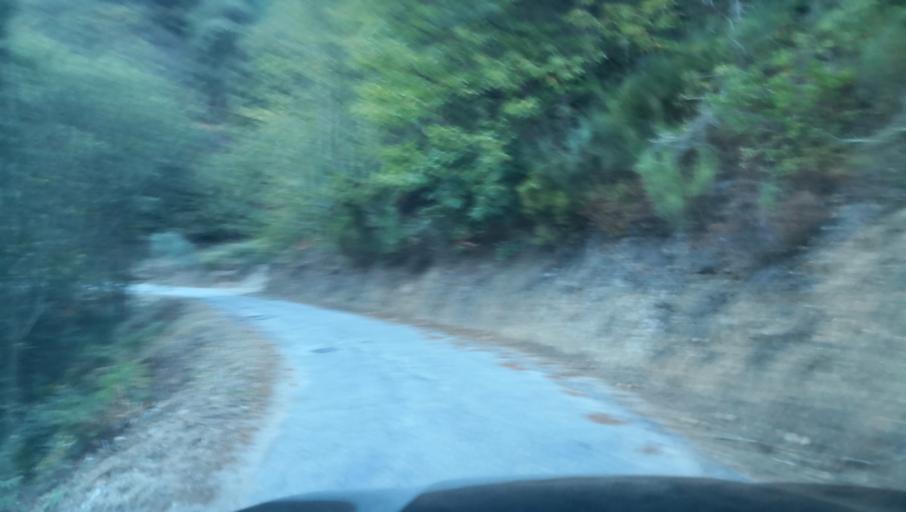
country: PT
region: Vila Real
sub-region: Santa Marta de Penaguiao
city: Santa Marta de Penaguiao
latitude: 41.2589
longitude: -7.8264
